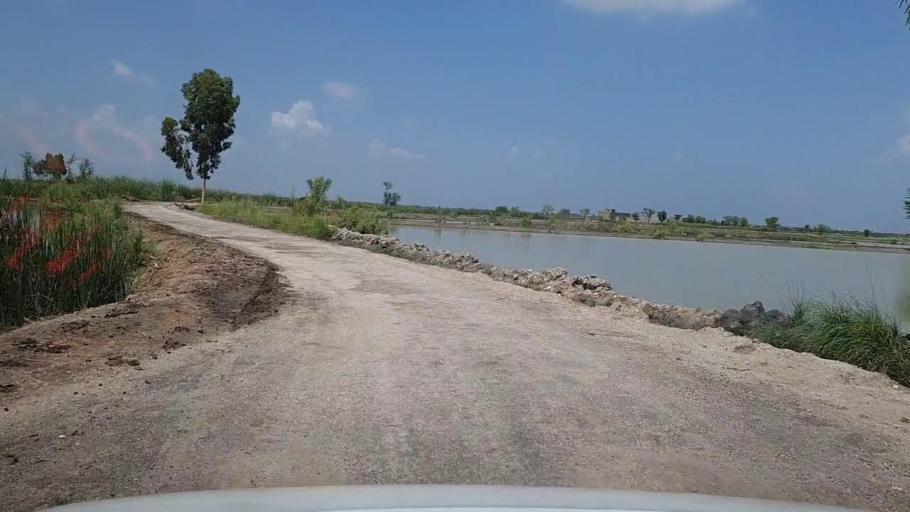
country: PK
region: Sindh
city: Bhiria
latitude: 26.9828
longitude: 68.2171
